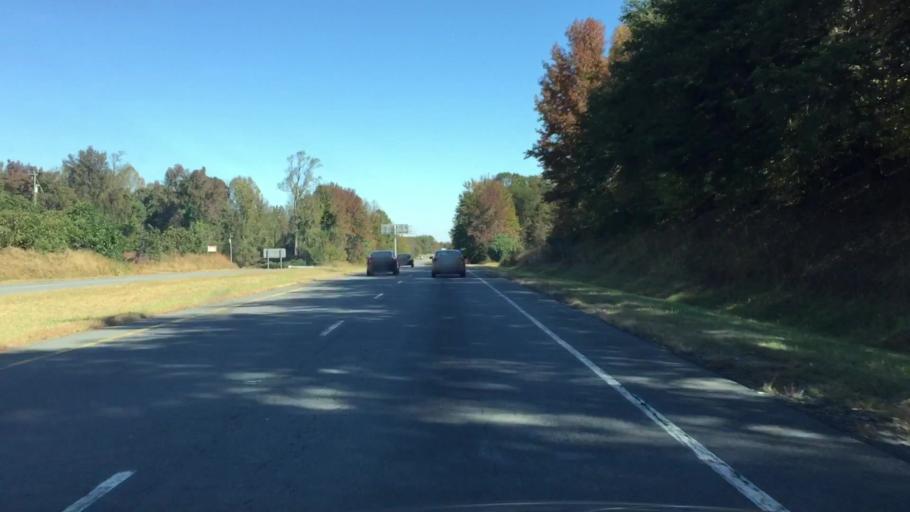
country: US
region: North Carolina
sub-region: Rockingham County
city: Reidsville
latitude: 36.2325
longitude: -79.6752
